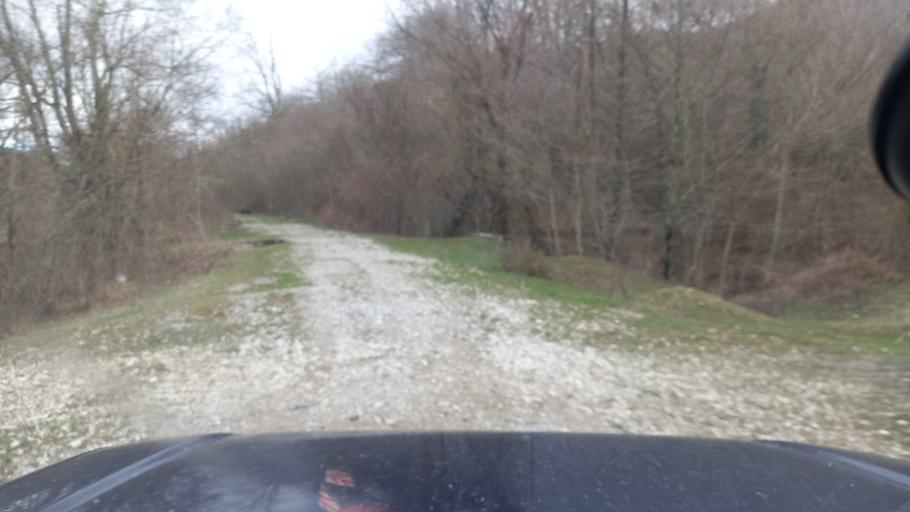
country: RU
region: Krasnodarskiy
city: Pshada
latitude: 44.4823
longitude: 38.4015
